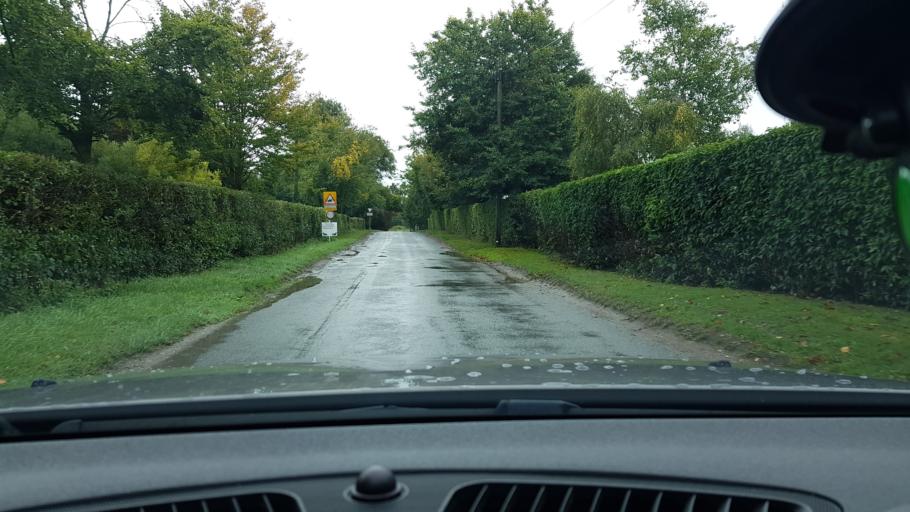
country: GB
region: England
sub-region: West Berkshire
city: Lambourn
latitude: 51.5288
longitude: -1.5247
